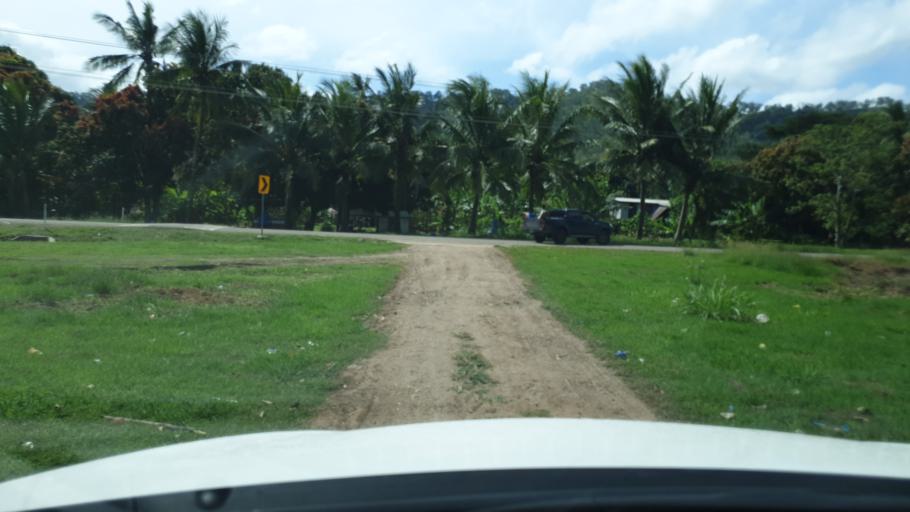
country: PG
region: Central Province
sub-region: Rigo
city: Kwikila
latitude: -9.8903
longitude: 147.5785
